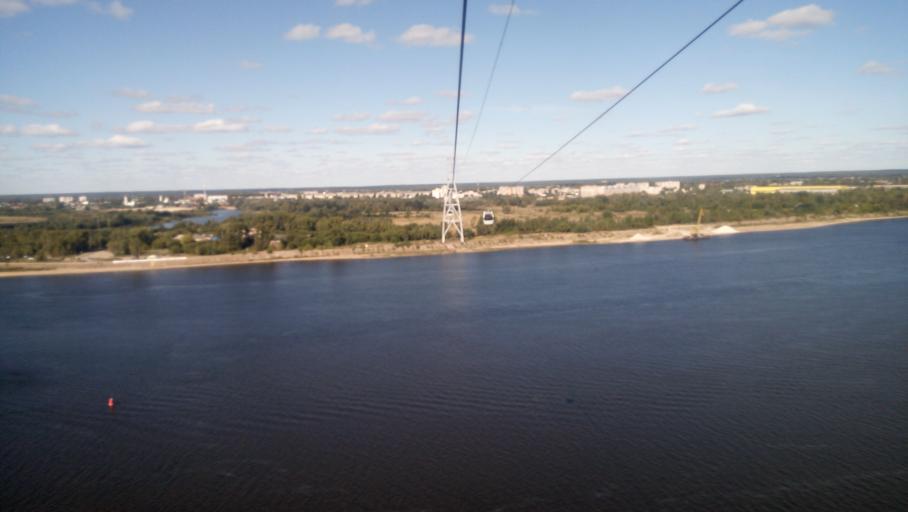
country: RU
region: Nizjnij Novgorod
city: Bor
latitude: 56.3351
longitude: 44.0472
